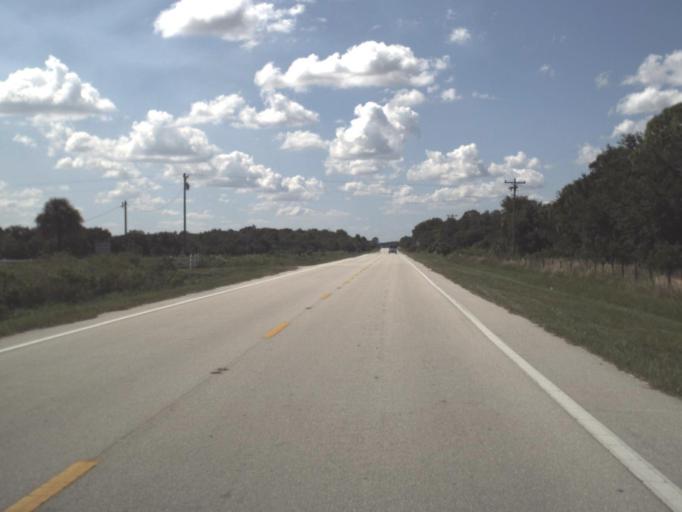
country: US
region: Florida
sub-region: Hendry County
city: Port LaBelle
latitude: 26.8129
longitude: -81.3293
